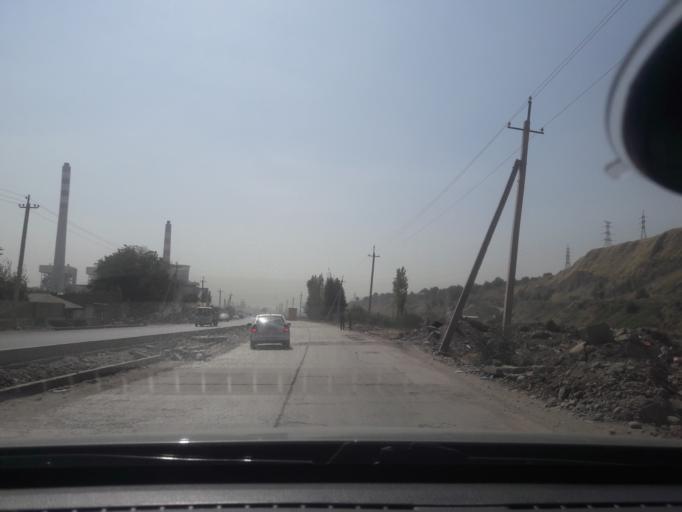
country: TJ
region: Dushanbe
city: Dushanbe
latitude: 38.6170
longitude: 68.7684
